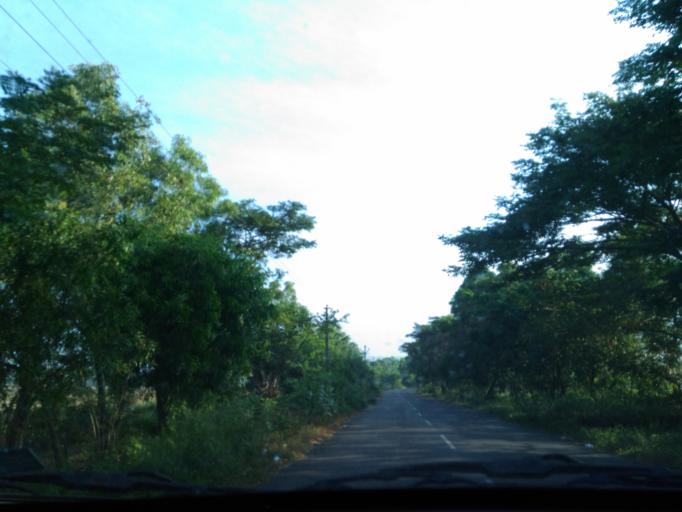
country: IN
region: Goa
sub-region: South Goa
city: Chinchinim
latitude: 15.2168
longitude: 73.9749
